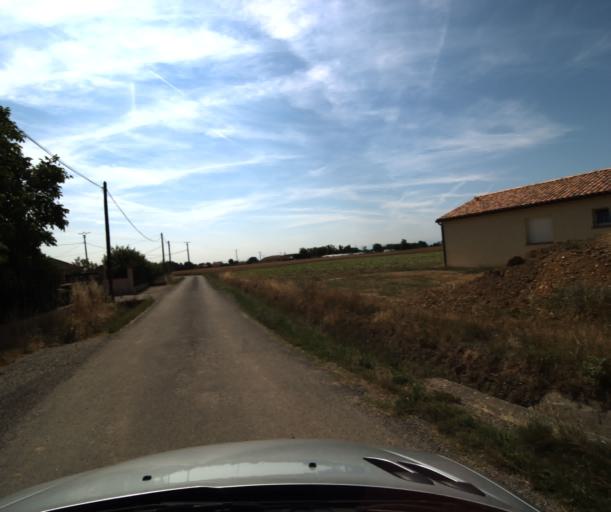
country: FR
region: Midi-Pyrenees
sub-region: Departement de la Haute-Garonne
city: Lherm
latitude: 43.4548
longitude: 1.1848
